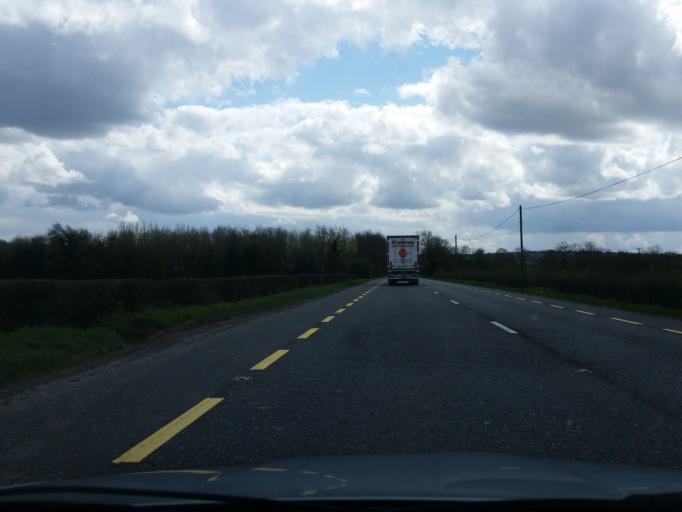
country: IE
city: Kentstown
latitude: 53.5930
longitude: -6.4648
